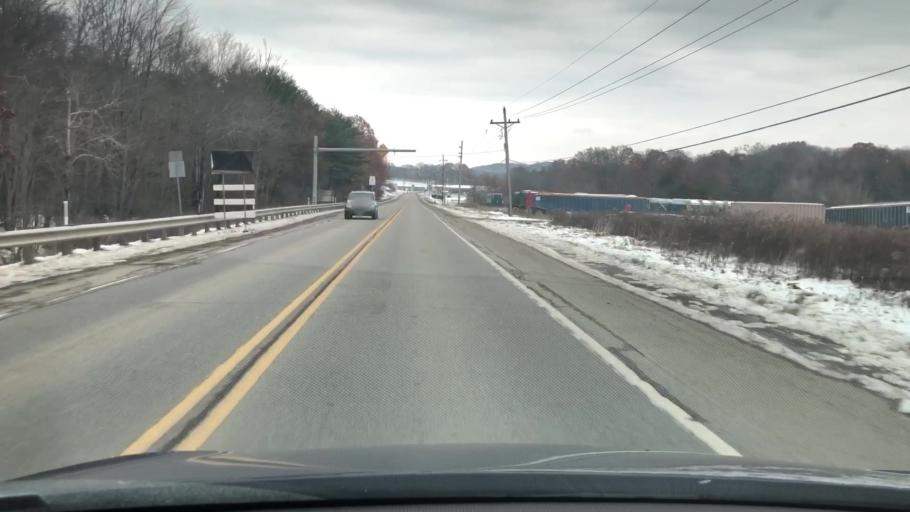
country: US
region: Pennsylvania
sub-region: Jefferson County
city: Brookville
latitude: 41.1615
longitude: -79.0982
